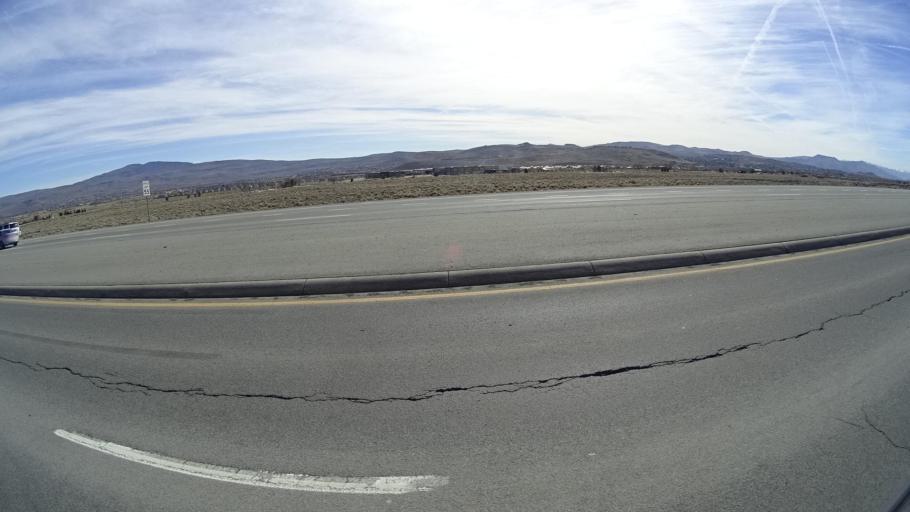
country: US
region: Nevada
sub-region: Washoe County
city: Spanish Springs
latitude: 39.6126
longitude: -119.7305
